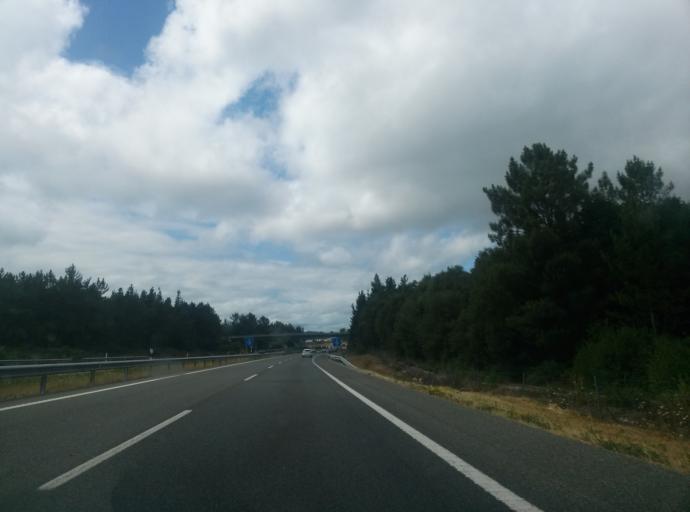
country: ES
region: Galicia
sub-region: Provincia de Lugo
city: Outeiro de Rei
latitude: 43.0991
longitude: -7.5976
